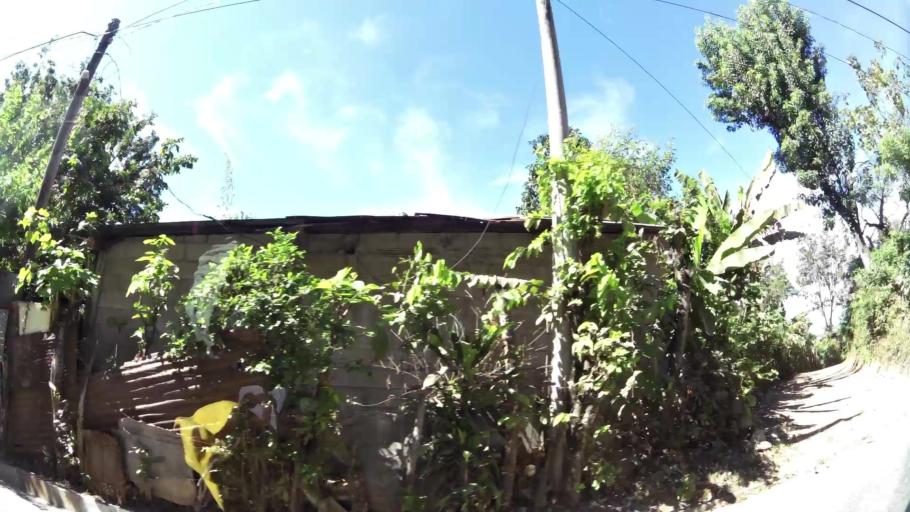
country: SV
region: San Salvador
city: Apopa
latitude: 13.8062
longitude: -89.1749
